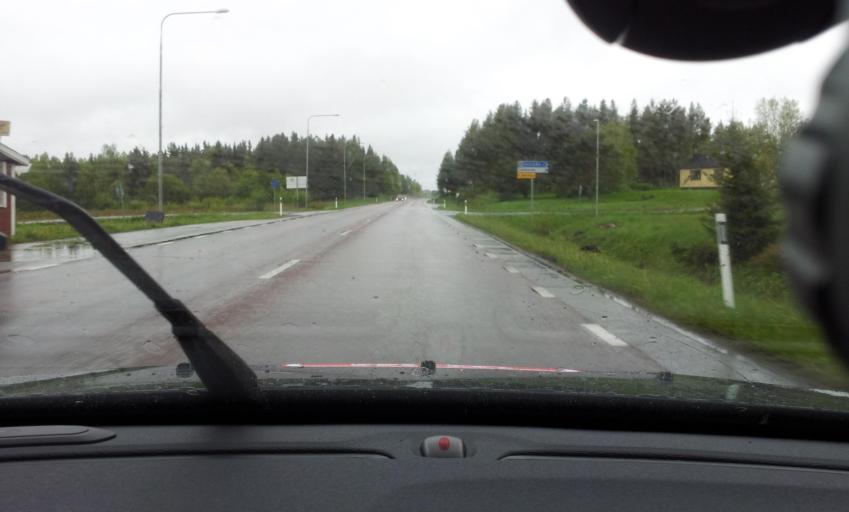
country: SE
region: Jaemtland
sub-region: Bergs Kommun
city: Hoverberg
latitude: 62.9269
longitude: 14.5359
